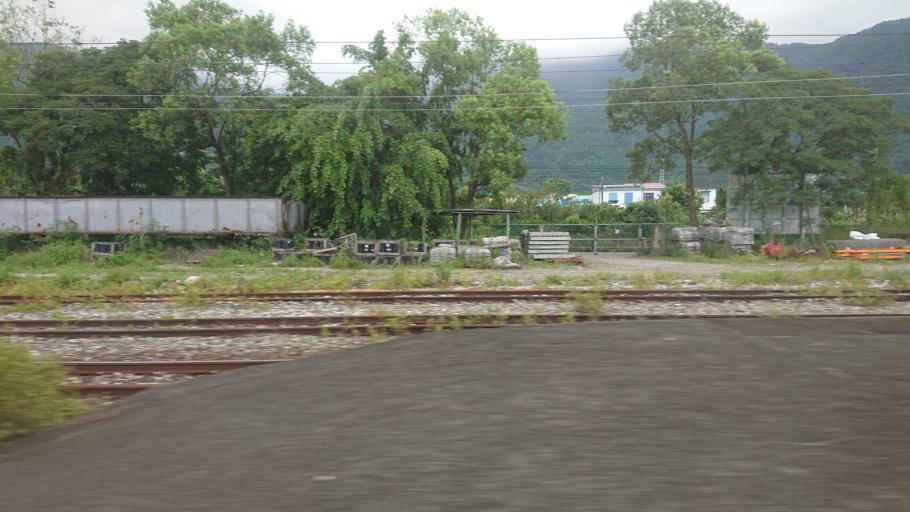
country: TW
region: Taiwan
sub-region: Hualien
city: Hualian
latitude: 23.7456
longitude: 121.4464
